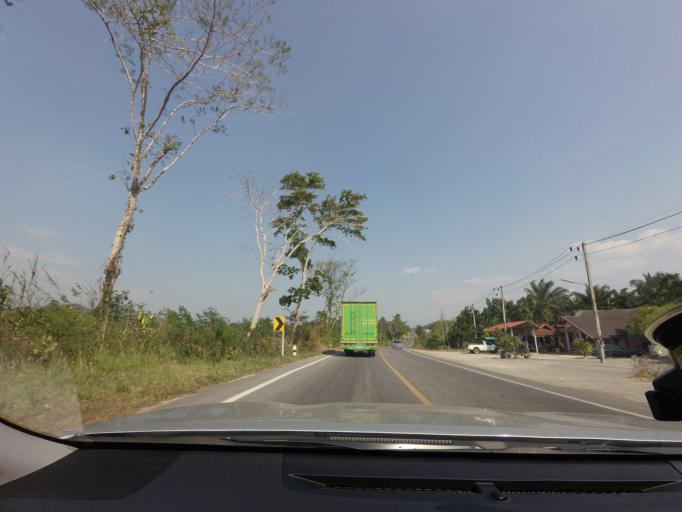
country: TH
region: Krabi
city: Plai Phraya
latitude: 8.5569
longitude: 98.8065
